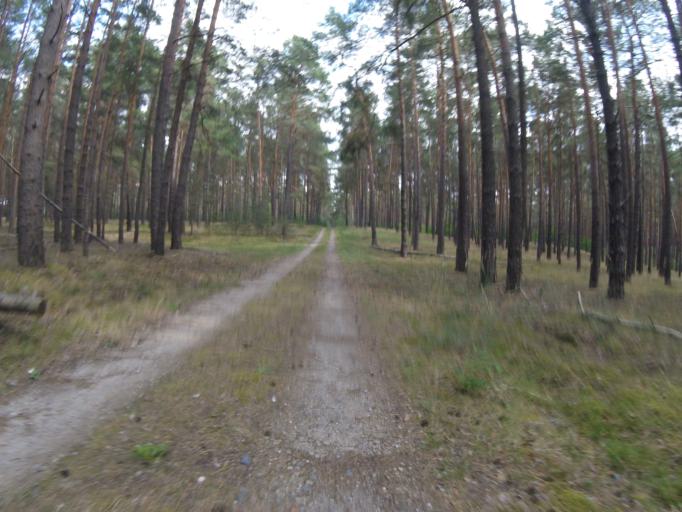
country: DE
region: Brandenburg
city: Halbe
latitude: 52.0620
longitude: 13.7580
